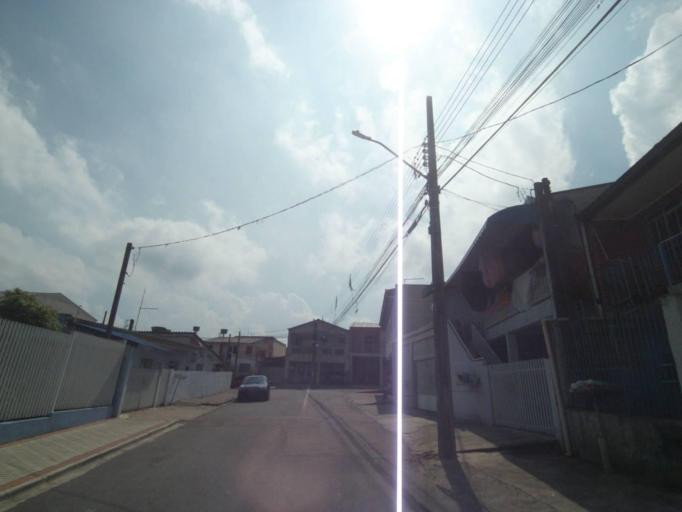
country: BR
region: Parana
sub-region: Curitiba
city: Curitiba
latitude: -25.5012
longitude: -49.3497
